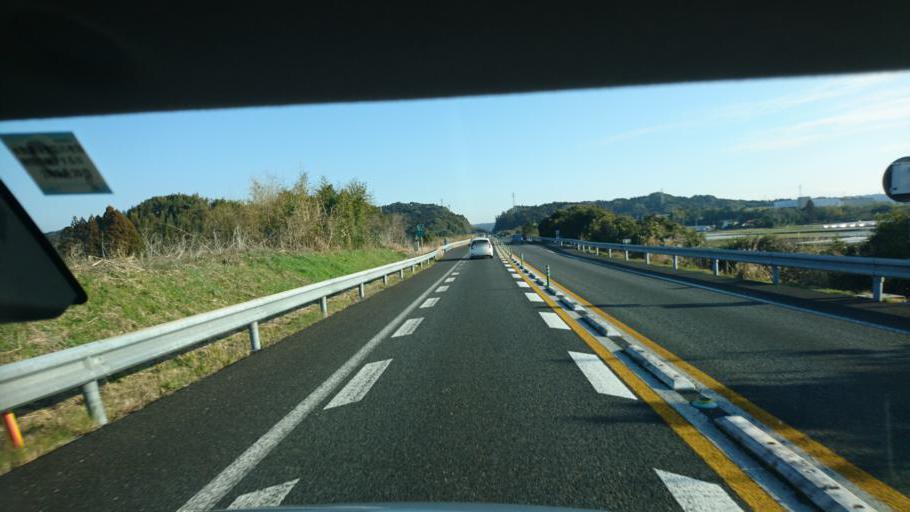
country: JP
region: Miyazaki
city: Miyazaki-shi
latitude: 31.9574
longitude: 131.3565
